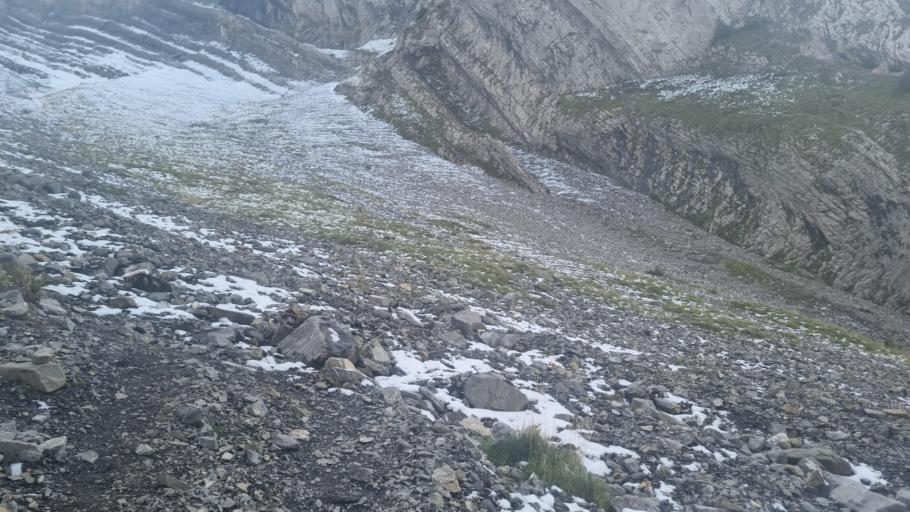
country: CH
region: Schwyz
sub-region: Bezirk March
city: Vorderthal
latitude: 47.0980
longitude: 8.9539
